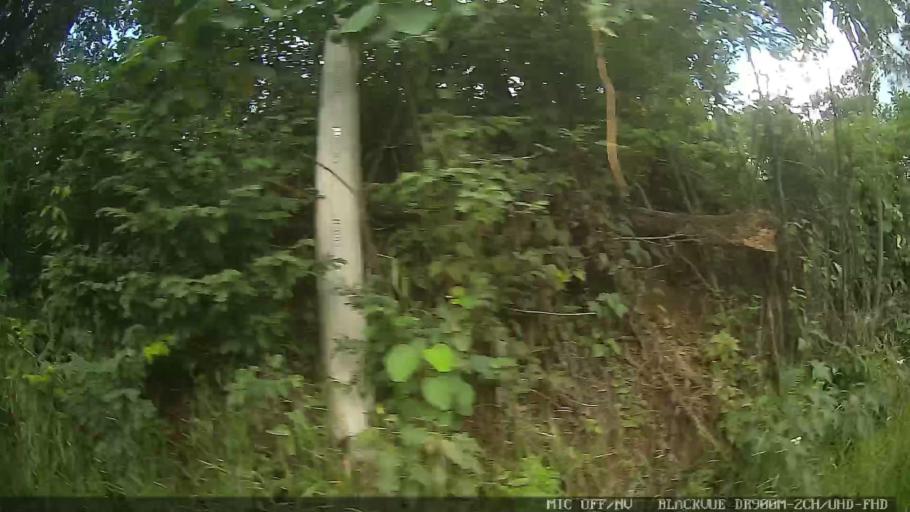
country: BR
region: Sao Paulo
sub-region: Braganca Paulista
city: Braganca Paulista
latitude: -22.9949
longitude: -46.4870
